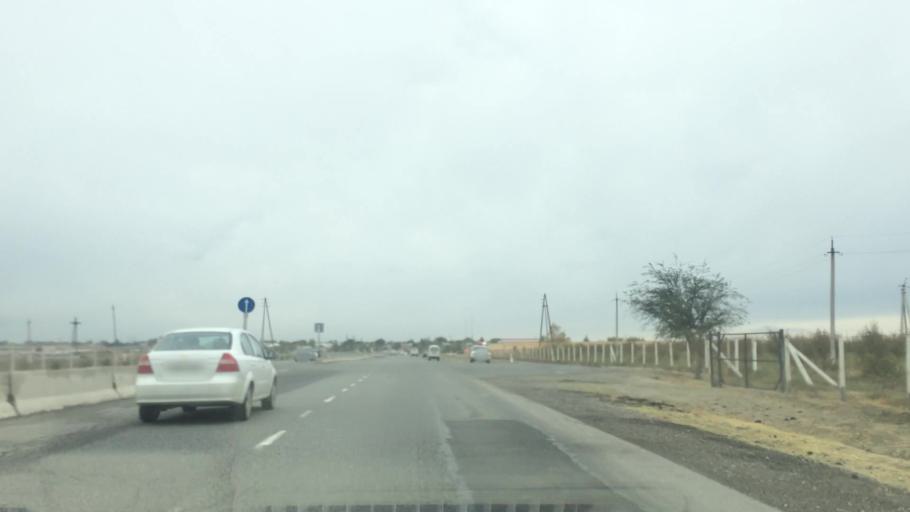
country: UZ
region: Samarqand
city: Bulung'ur
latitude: 39.7761
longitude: 67.2864
